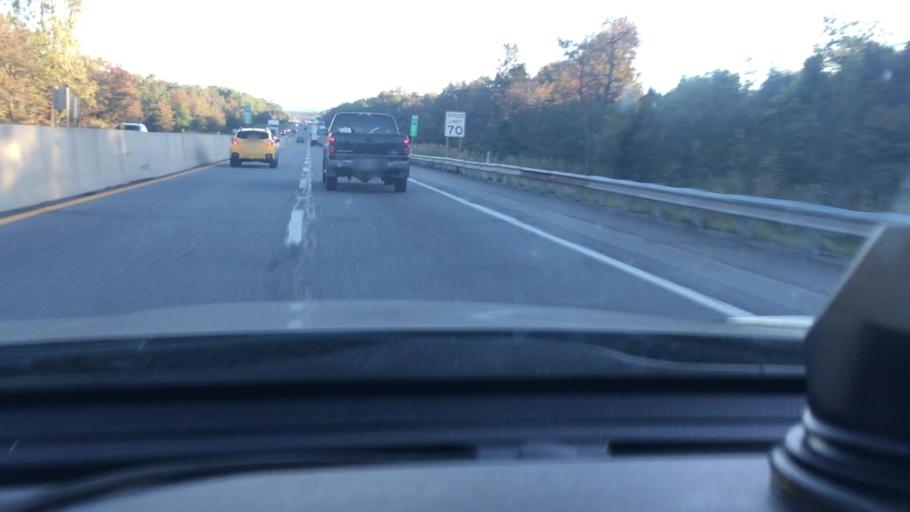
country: US
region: Pennsylvania
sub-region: Carbon County
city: Towamensing Trails
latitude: 40.9534
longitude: -75.6338
